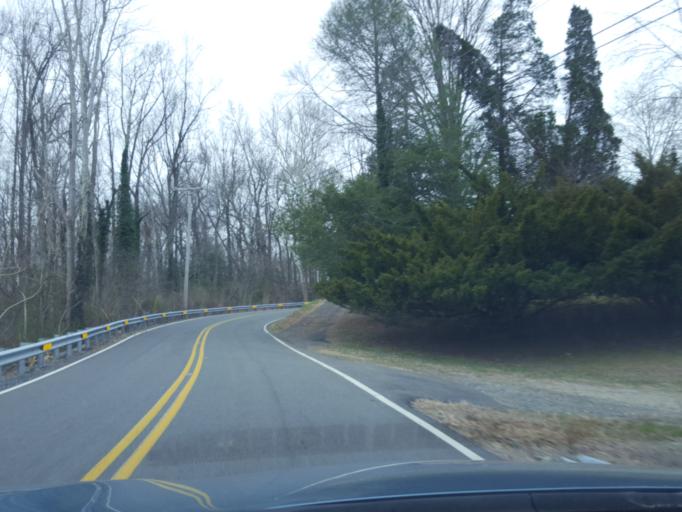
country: US
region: Maryland
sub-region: Calvert County
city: Prince Frederick
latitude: 38.4874
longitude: -76.5771
